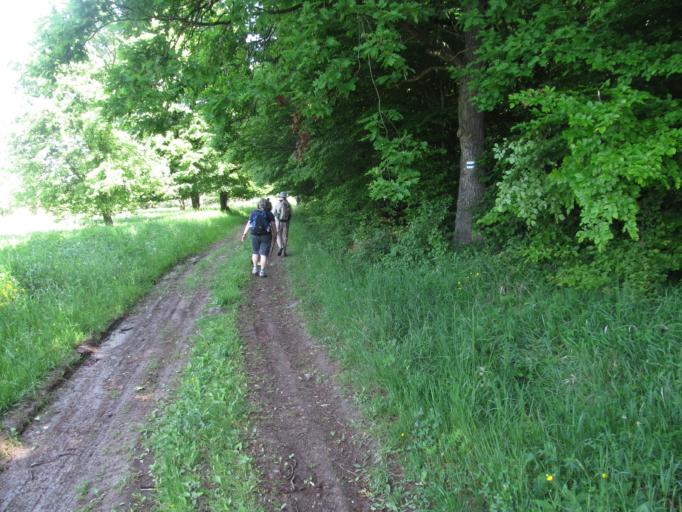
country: HU
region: Borsod-Abauj-Zemplen
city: Gonc
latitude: 48.5600
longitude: 21.4231
